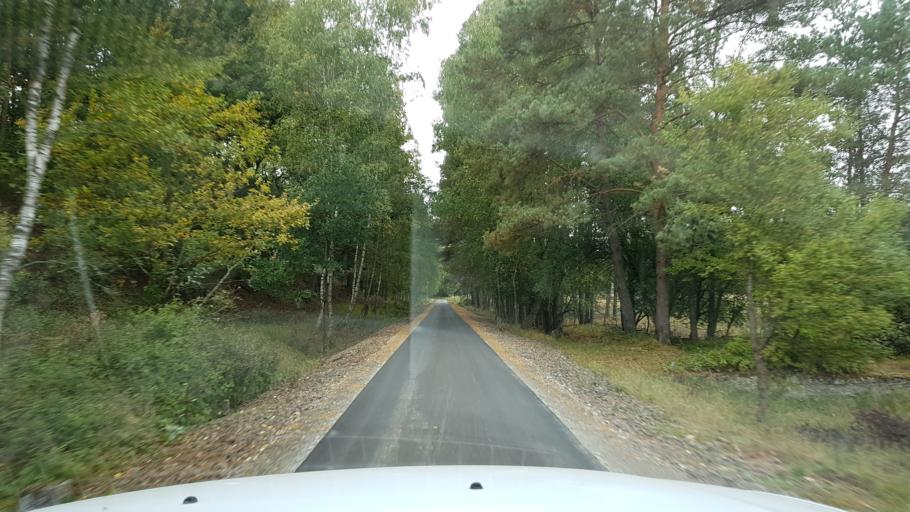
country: PL
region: West Pomeranian Voivodeship
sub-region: Powiat gryfinski
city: Cedynia
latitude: 52.8363
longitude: 14.2746
